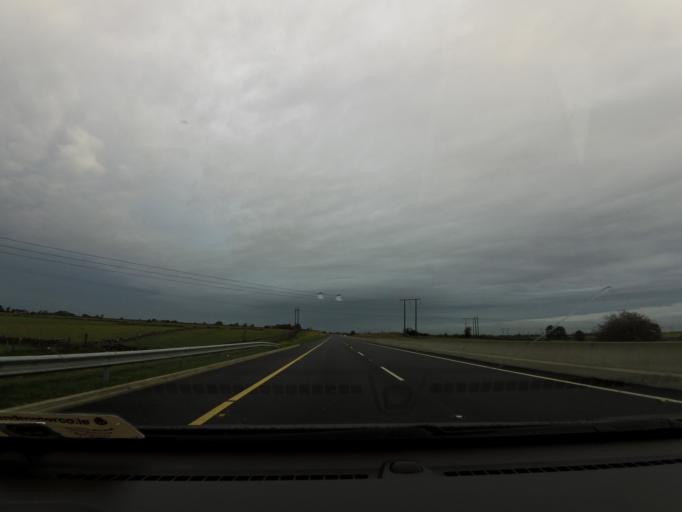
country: IE
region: Connaught
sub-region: County Galway
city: Tuam
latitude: 53.4769
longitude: -8.8638
